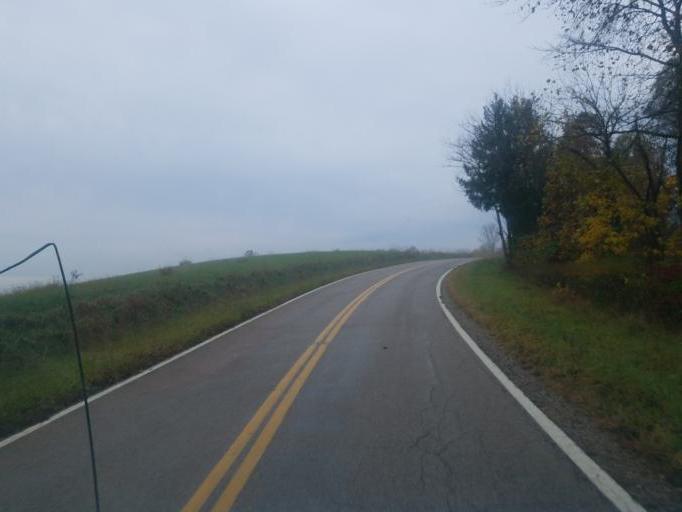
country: US
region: Ohio
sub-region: Morgan County
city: McConnelsville
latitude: 39.5135
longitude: -81.9136
